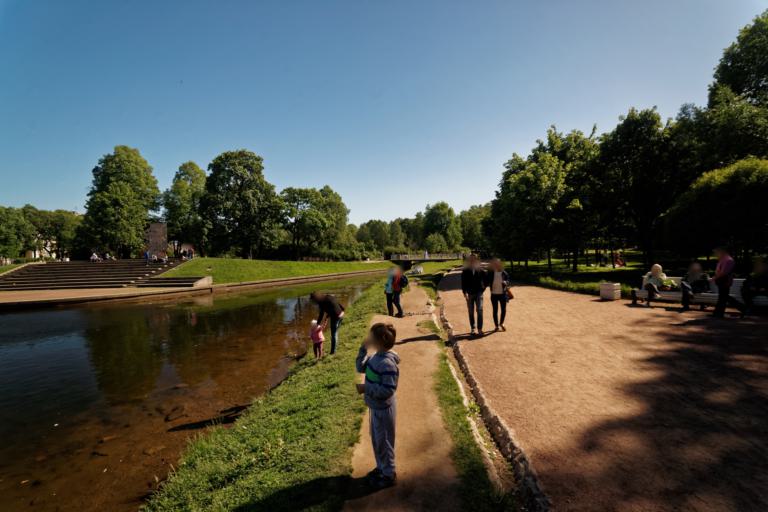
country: RU
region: St.-Petersburg
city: Centralniy
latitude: 59.9458
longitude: 30.3751
